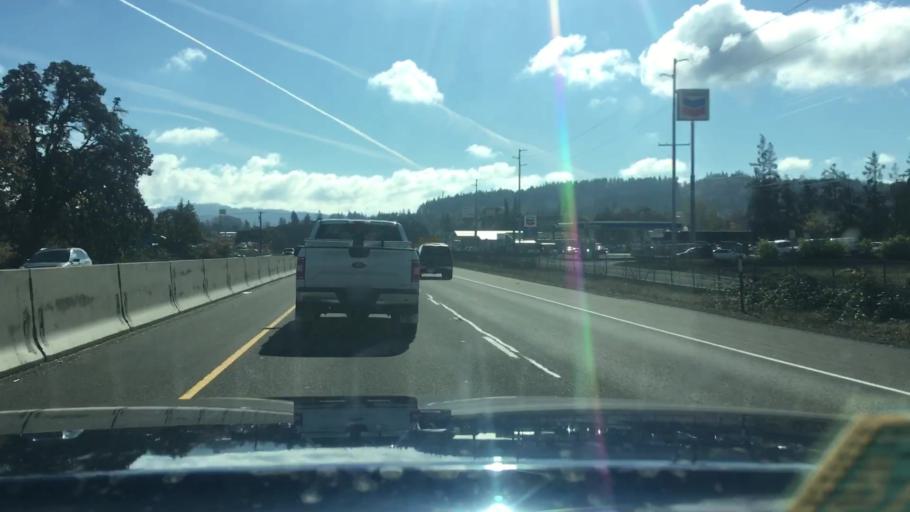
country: US
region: Oregon
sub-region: Lane County
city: Springfield
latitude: 44.0226
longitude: -123.0274
